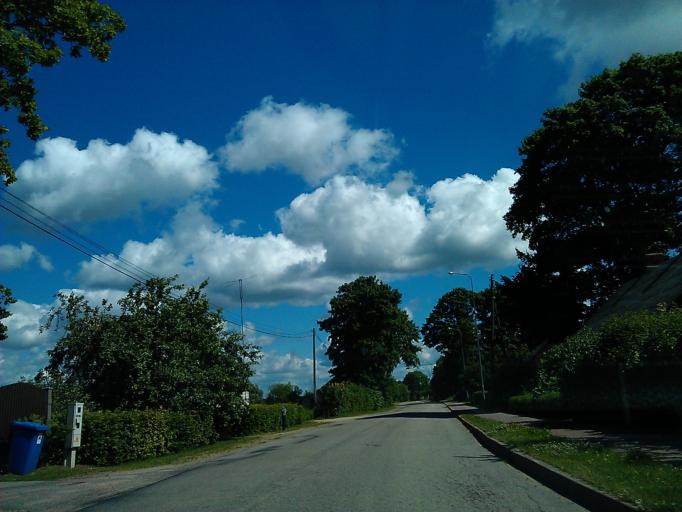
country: LV
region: Varaklani
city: Varaklani
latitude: 56.6049
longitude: 26.7385
